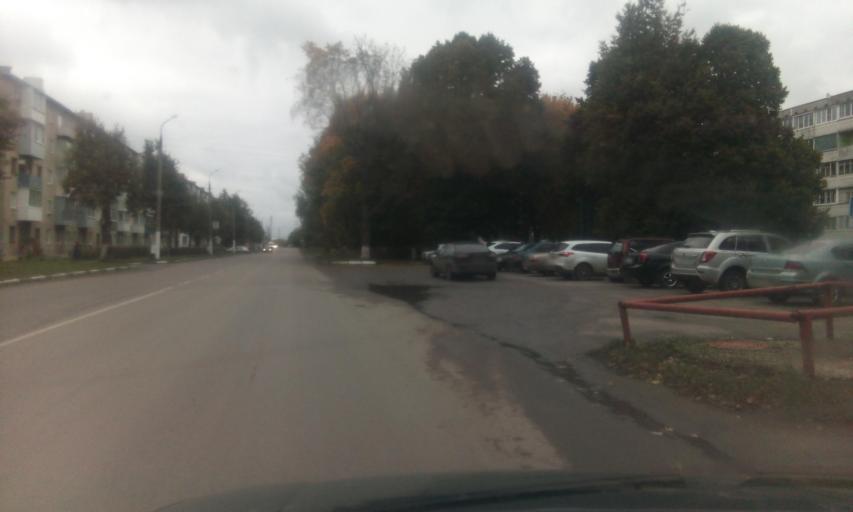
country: RU
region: Tula
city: Uzlovaya
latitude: 53.9822
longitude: 38.1577
